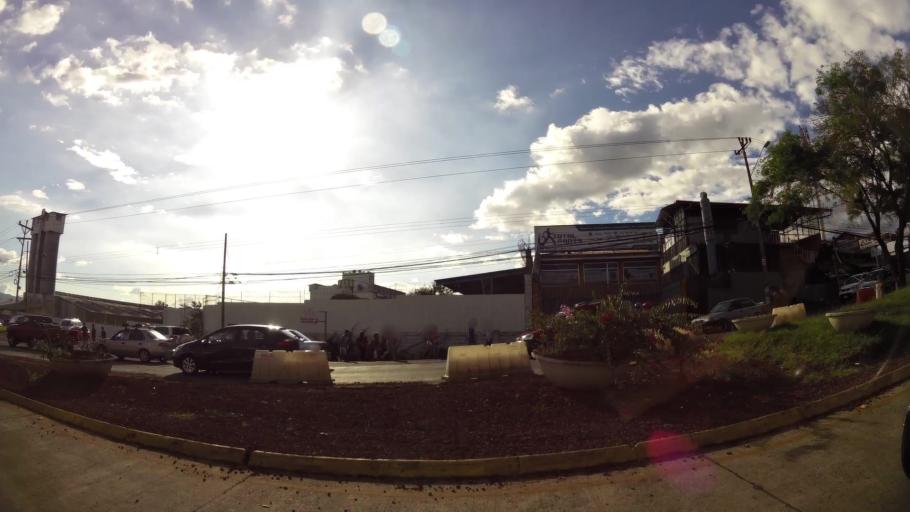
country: CR
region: Alajuela
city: Alajuela
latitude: 10.0097
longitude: -84.2132
